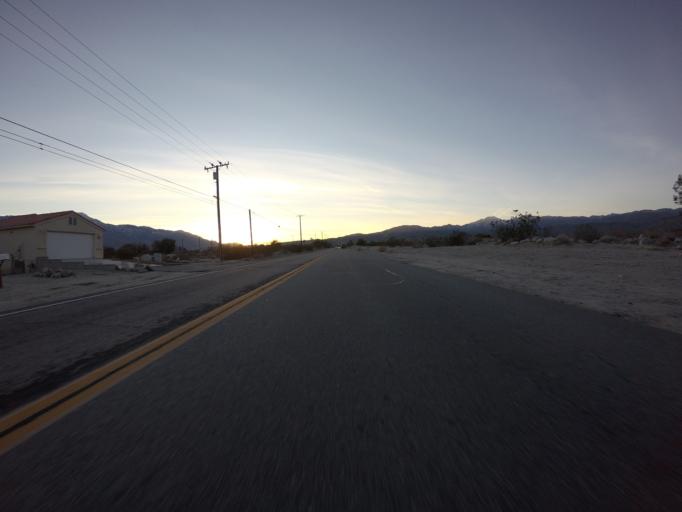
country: US
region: California
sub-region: Riverside County
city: Desert Hot Springs
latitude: 33.9614
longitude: -116.5340
